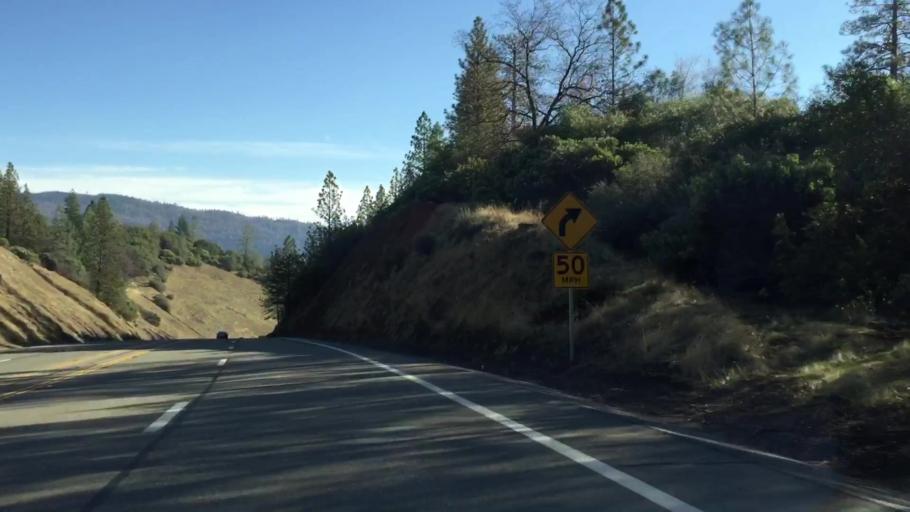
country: US
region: California
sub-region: Butte County
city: Paradise
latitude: 39.6737
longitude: -121.5302
